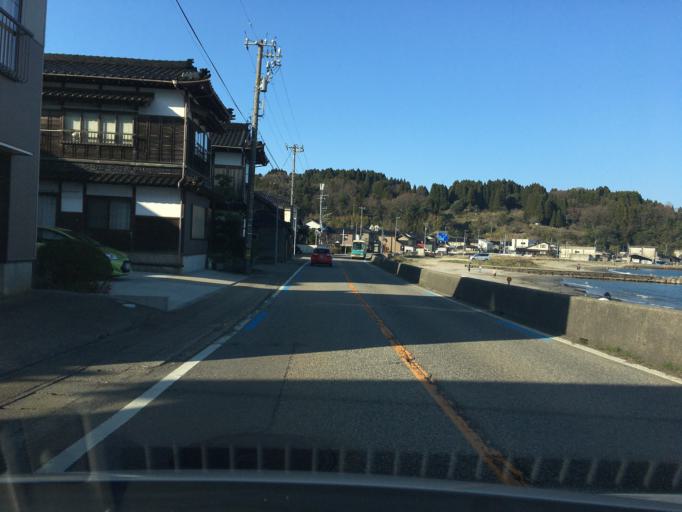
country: JP
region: Toyama
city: Himi
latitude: 36.9103
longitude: 137.0174
